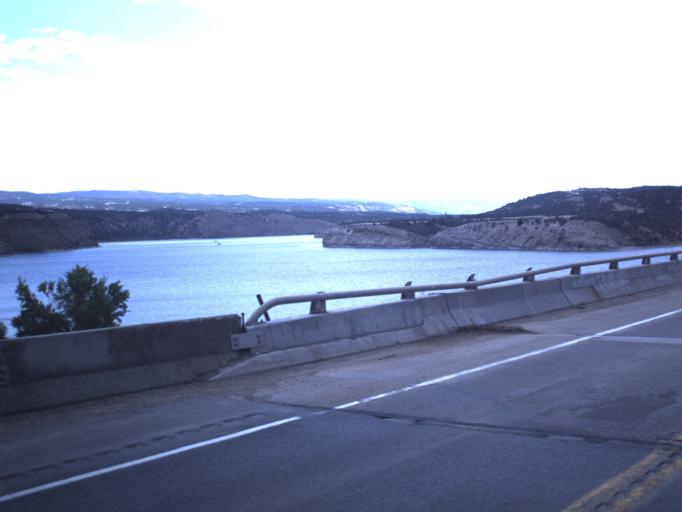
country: US
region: Utah
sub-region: Duchesne County
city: Duchesne
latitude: 40.1731
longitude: -110.4934
